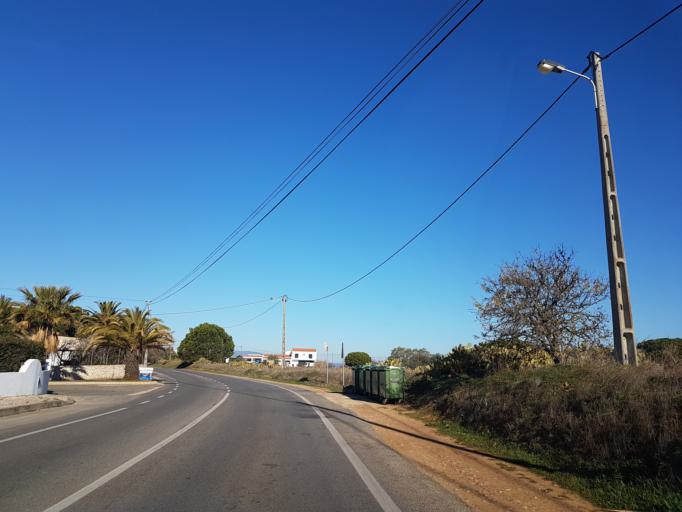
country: PT
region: Faro
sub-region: Lagoa
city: Carvoeiro
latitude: 37.0989
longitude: -8.4424
